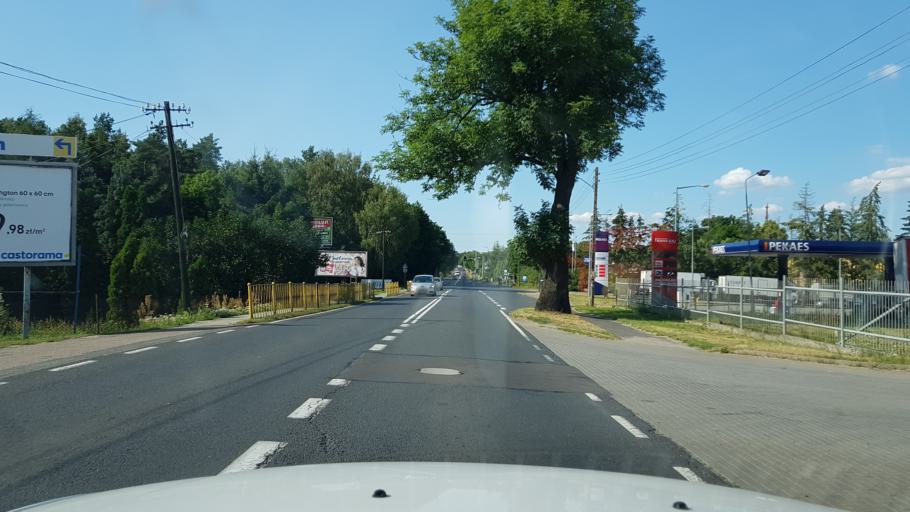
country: PL
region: West Pomeranian Voivodeship
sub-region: Powiat gryfinski
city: Stare Czarnowo
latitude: 53.3525
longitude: 14.7448
